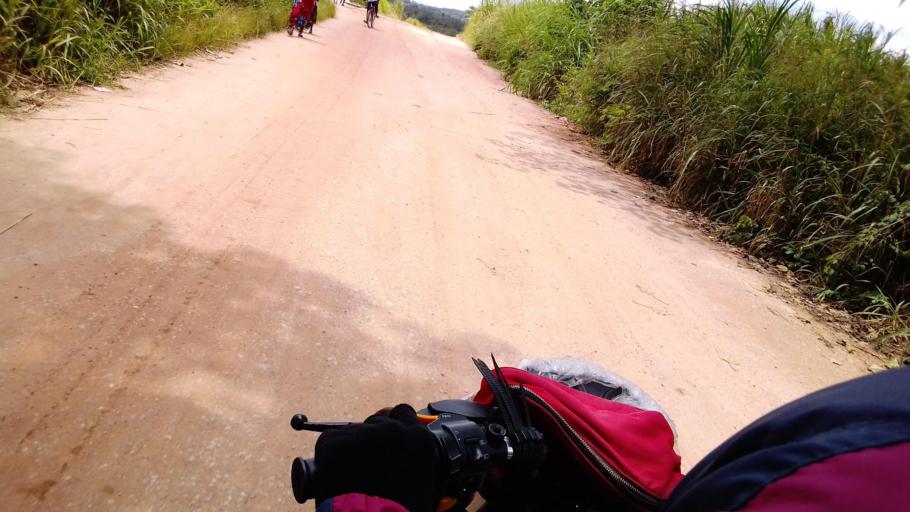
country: SL
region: Eastern Province
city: Koidu
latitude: 8.6692
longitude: -10.9784
